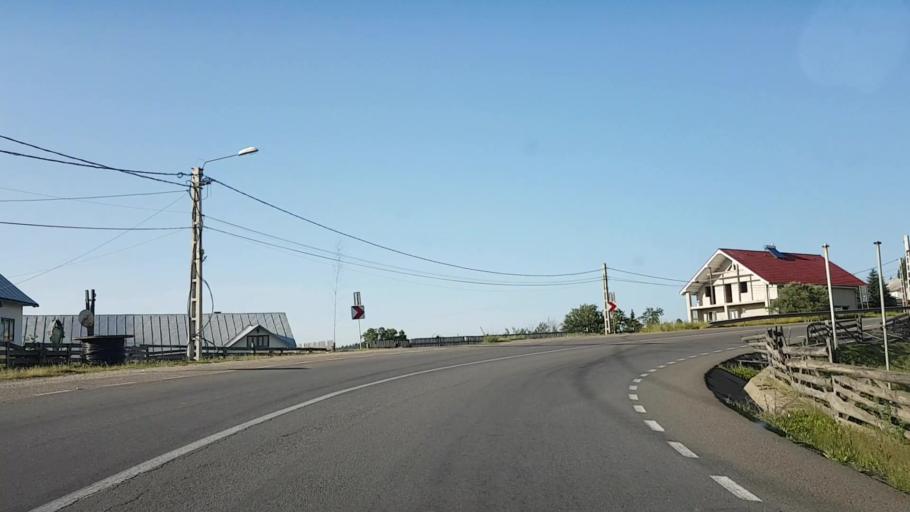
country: RO
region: Bistrita-Nasaud
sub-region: Comuna Lunca Ilvei
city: Lunca Ilvei
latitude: 47.2362
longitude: 25.0012
